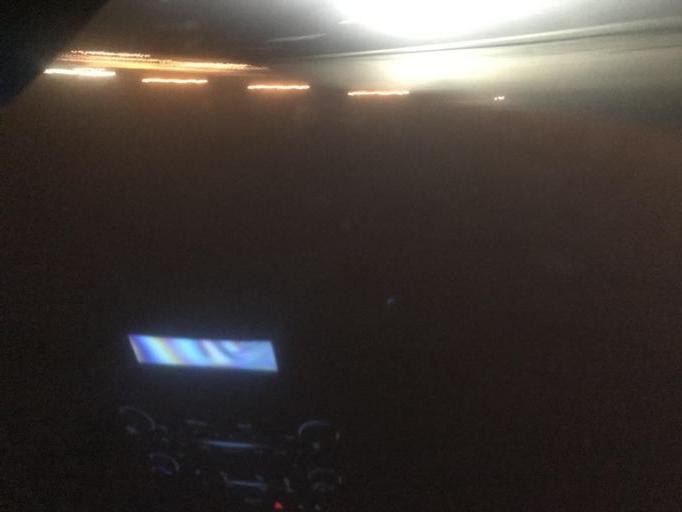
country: SA
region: Ar Riyad
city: Riyadh
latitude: 24.7618
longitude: 46.5865
